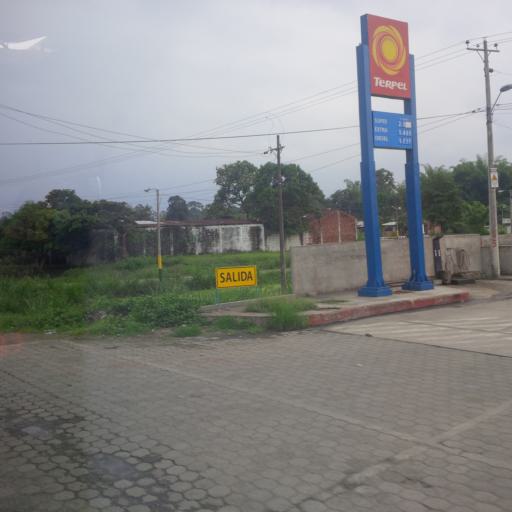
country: EC
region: Canar
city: La Troncal
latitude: -2.3379
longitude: -79.3905
